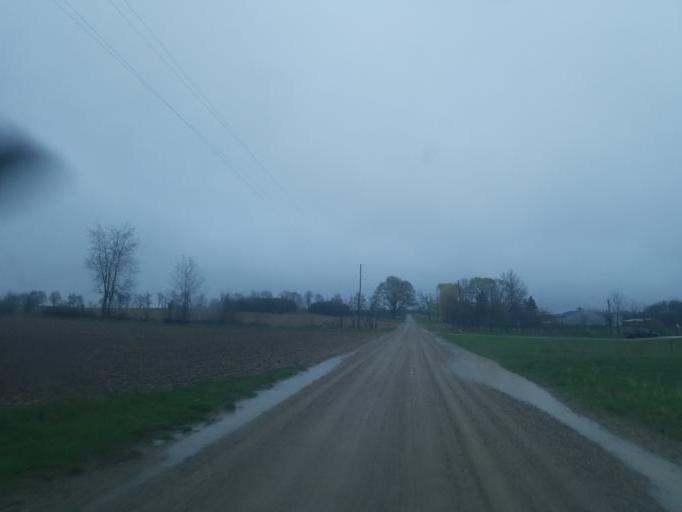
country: US
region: Michigan
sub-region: Montcalm County
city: Edmore
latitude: 43.4660
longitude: -85.0211
